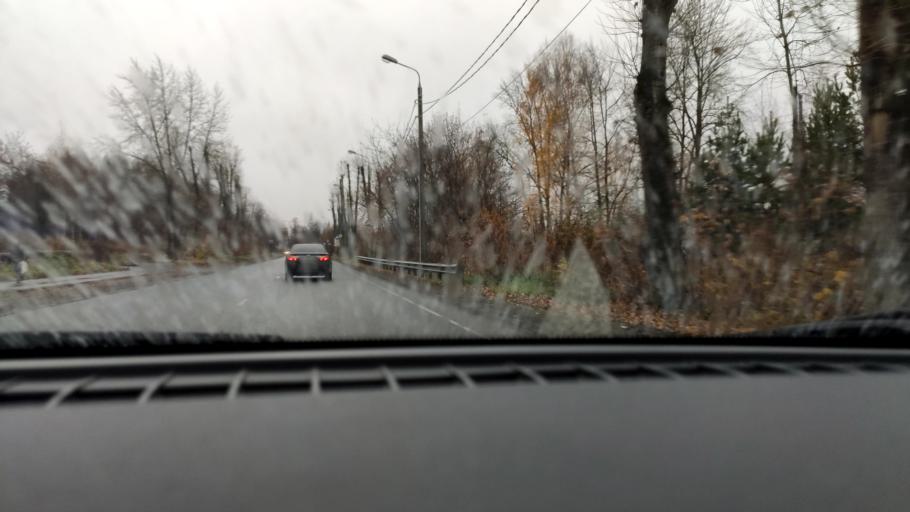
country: RU
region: Perm
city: Kondratovo
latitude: 57.9691
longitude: 56.1278
